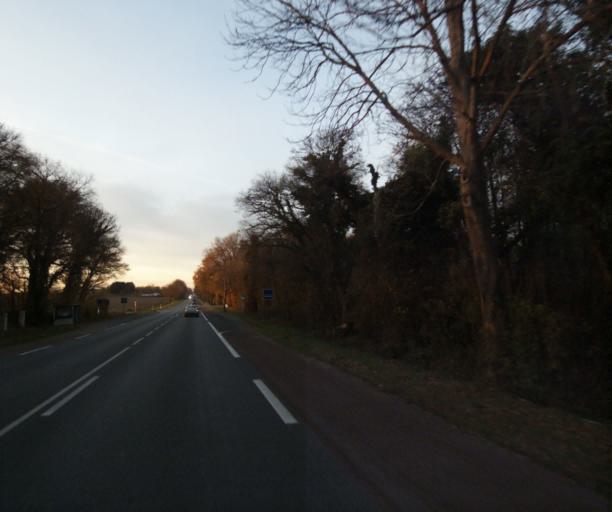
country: FR
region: Poitou-Charentes
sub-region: Departement de la Charente-Maritime
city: Saint-Georges-des-Coteaux
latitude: 45.7716
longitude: -0.6888
